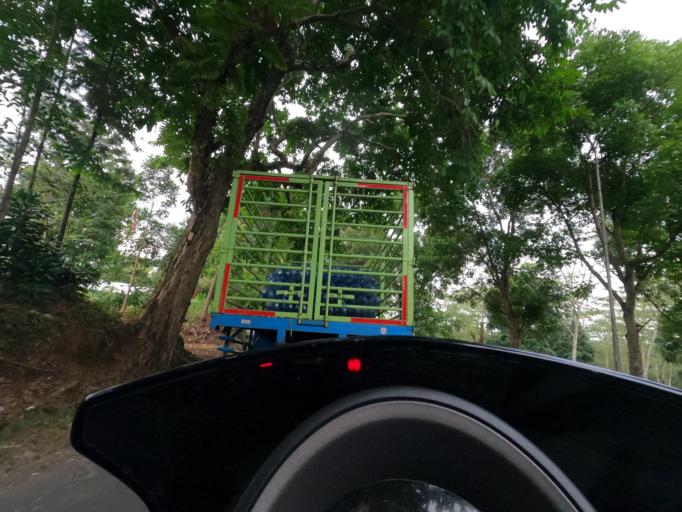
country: ID
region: West Java
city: Lembang
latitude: -6.6751
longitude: 107.6954
